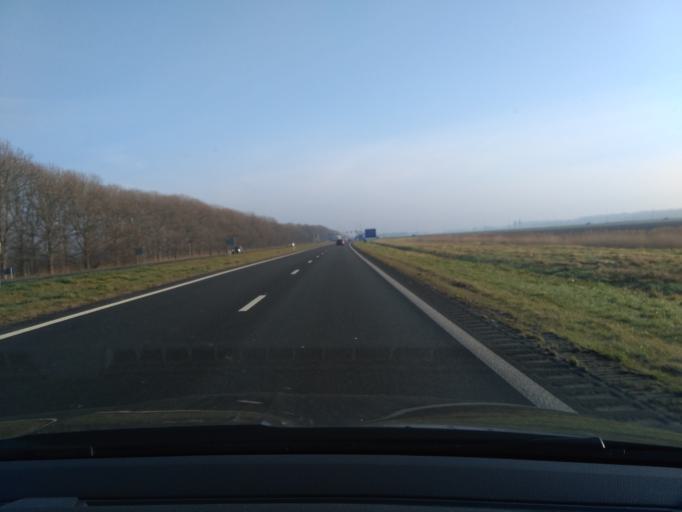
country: NL
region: Flevoland
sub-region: Gemeente Zeewolde
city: Zeewolde
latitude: 52.3899
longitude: 5.5659
